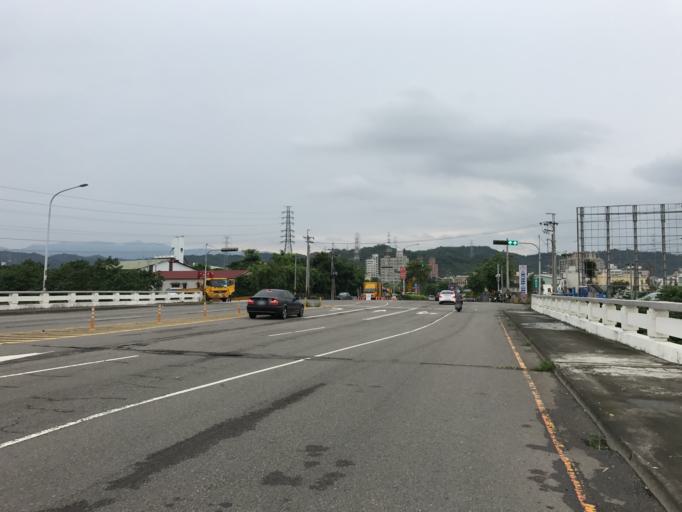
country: TW
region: Taiwan
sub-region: Taichung City
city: Taichung
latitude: 24.0735
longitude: 120.6925
